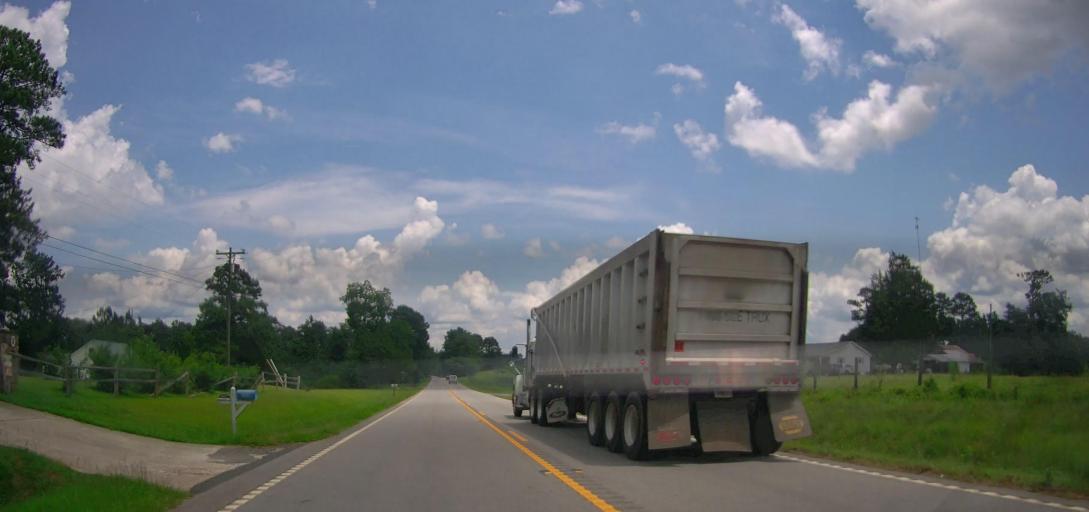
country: US
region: Georgia
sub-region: Meriwether County
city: Greenville
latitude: 32.9875
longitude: -84.6193
